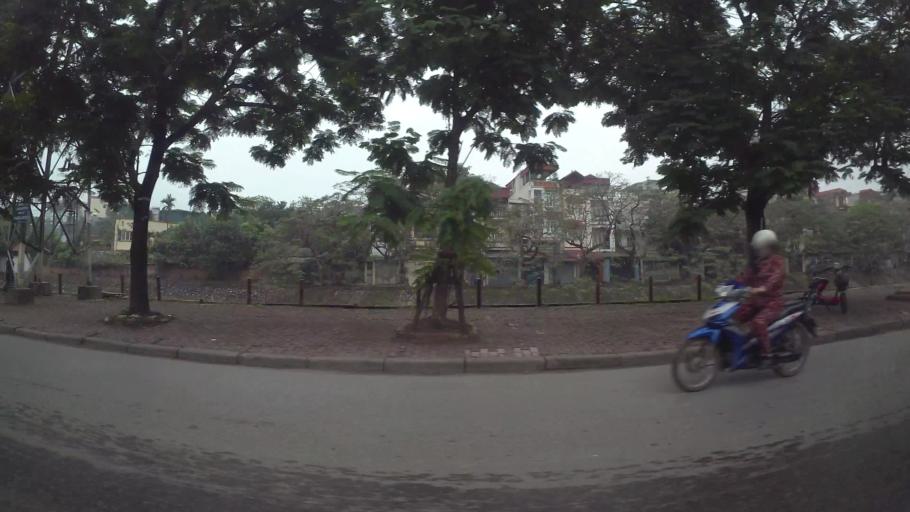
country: VN
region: Ha Noi
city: Hai BaTrung
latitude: 20.9862
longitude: 105.8636
